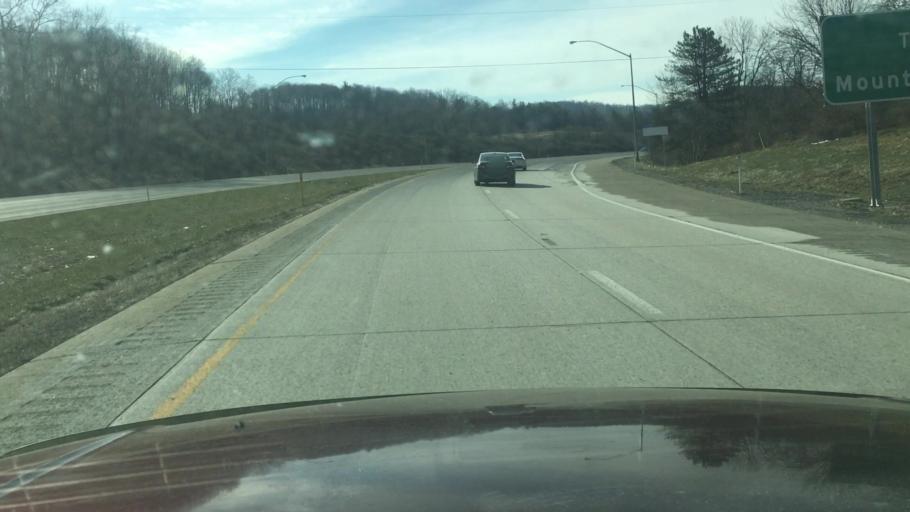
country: US
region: West Virginia
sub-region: Monongalia County
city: Star City
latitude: 39.7395
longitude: -80.0586
